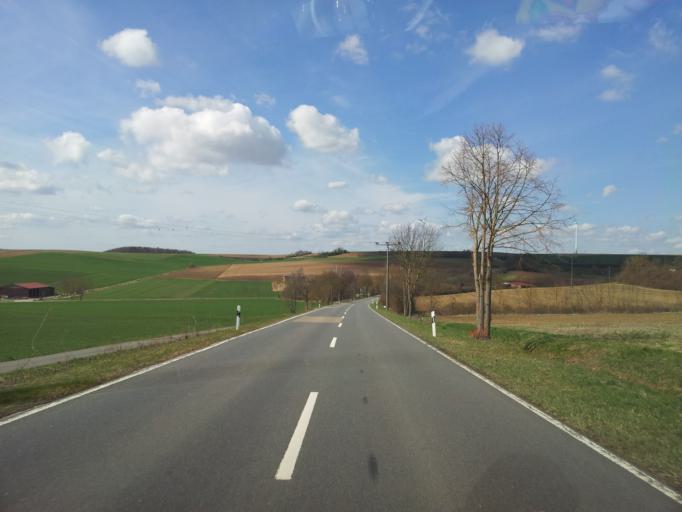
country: DE
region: Baden-Wuerttemberg
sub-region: Regierungsbezirk Stuttgart
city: Grossrinderfeld
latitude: 49.6982
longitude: 9.7835
